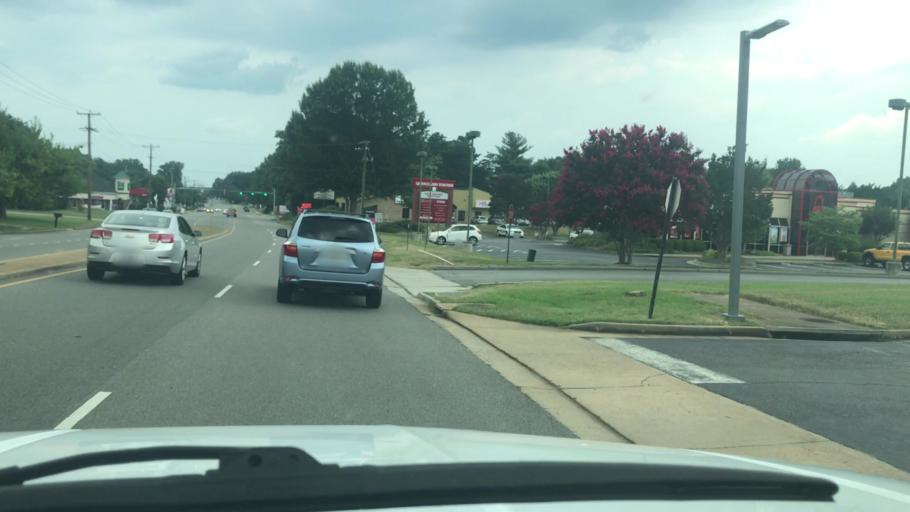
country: US
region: Virginia
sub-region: Henrico County
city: Tuckahoe
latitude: 37.6047
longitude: -77.5695
